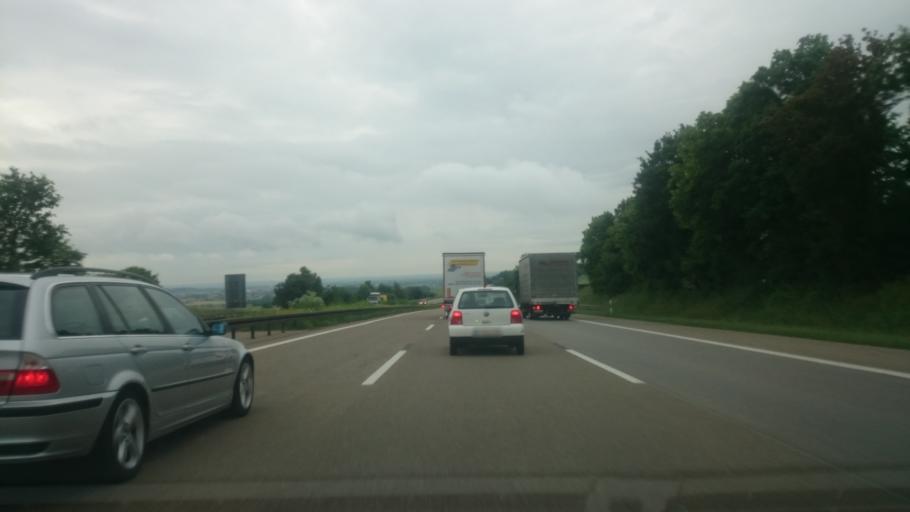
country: DE
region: Bavaria
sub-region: Upper Bavaria
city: Stammham
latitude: 48.8341
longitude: 11.4710
